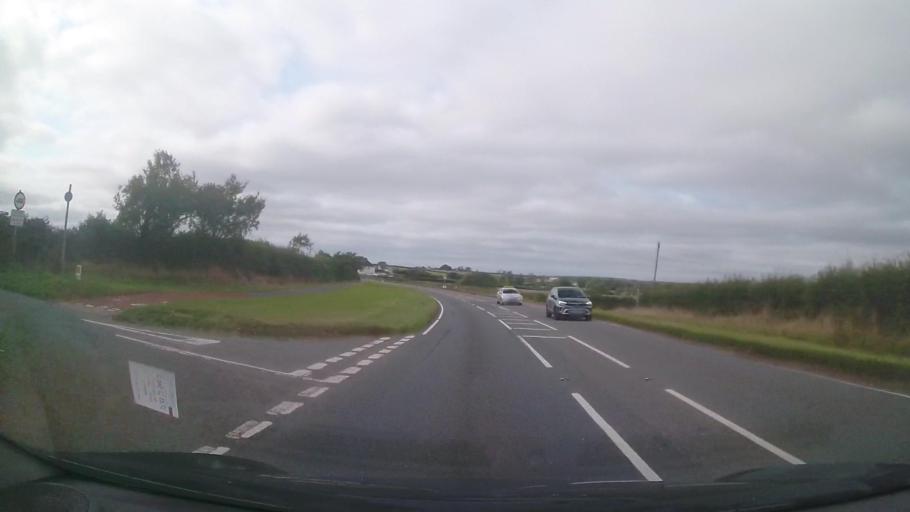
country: GB
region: Wales
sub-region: Pembrokeshire
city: Neyland
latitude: 51.7247
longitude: -4.9715
